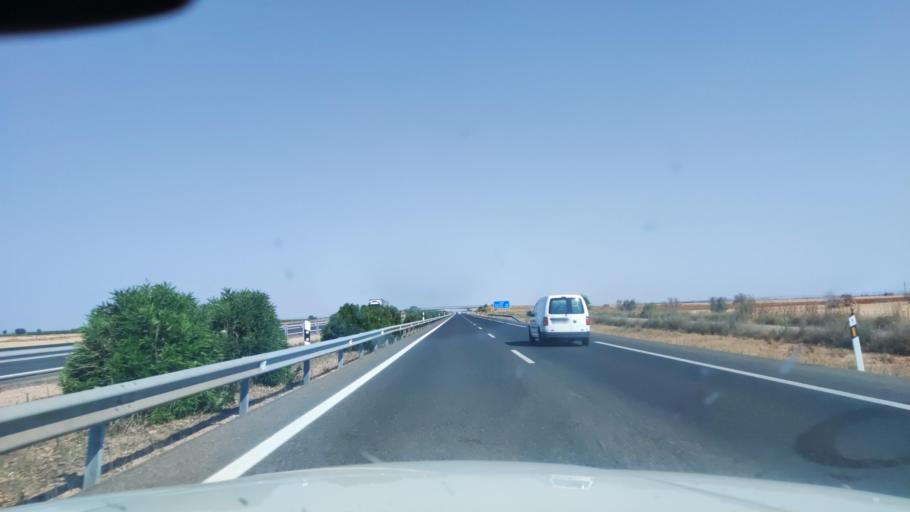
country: ES
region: Castille-La Mancha
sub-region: Provincia de Albacete
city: Montalvos
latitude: 39.1571
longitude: -2.0736
